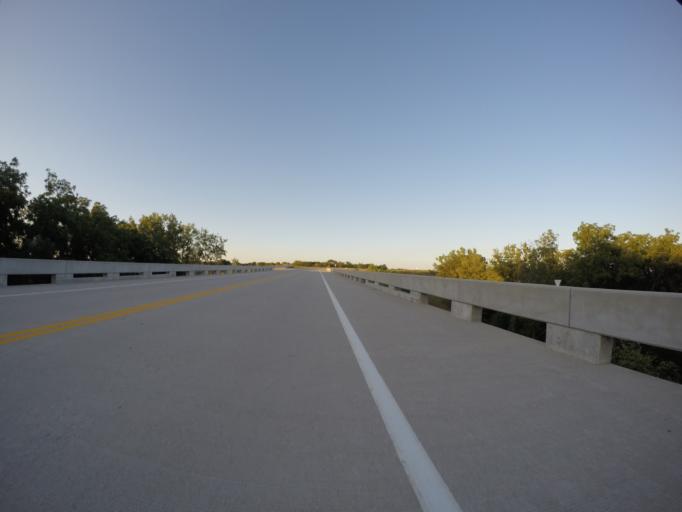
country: US
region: Kansas
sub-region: Riley County
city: Ogden
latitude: 39.1194
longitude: -96.6994
